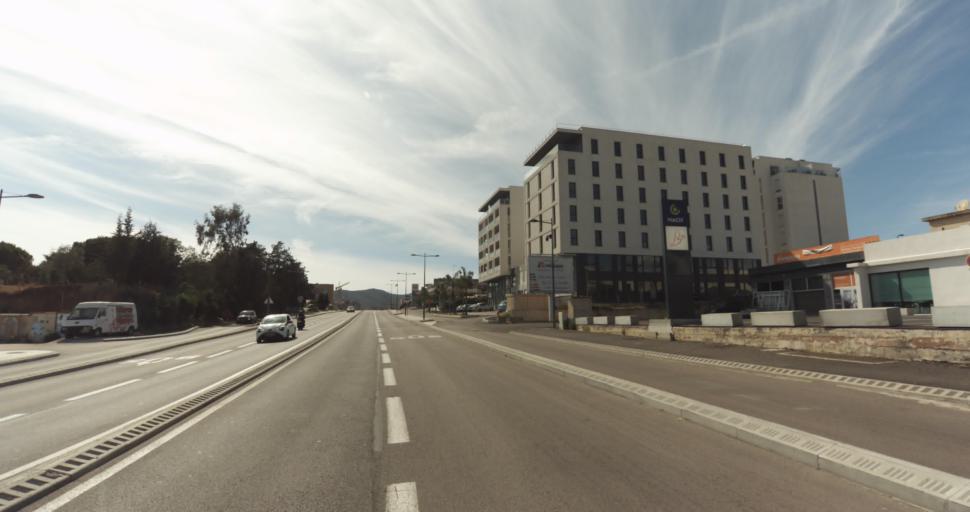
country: FR
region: Corsica
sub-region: Departement de la Corse-du-Sud
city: Ajaccio
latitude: 41.9449
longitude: 8.7574
